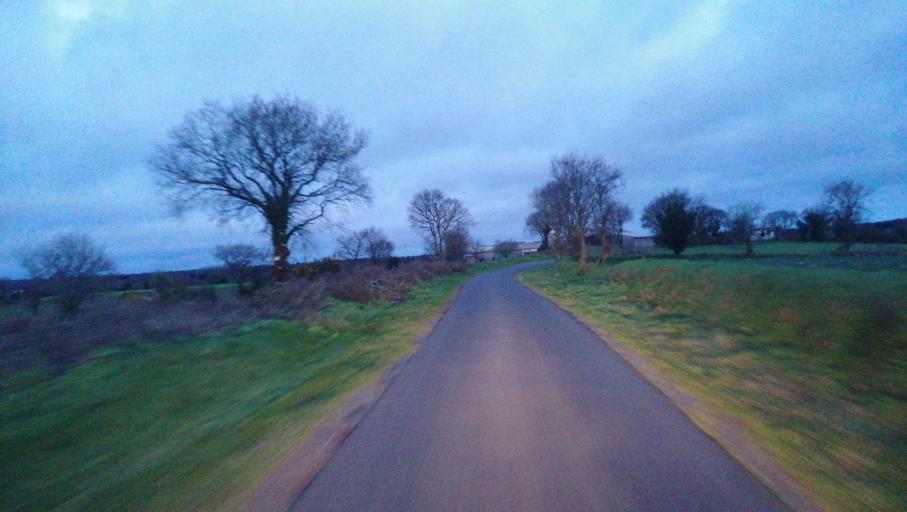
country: FR
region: Brittany
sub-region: Departement des Cotes-d'Armor
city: Plehedel
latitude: 48.6710
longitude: -3.0375
